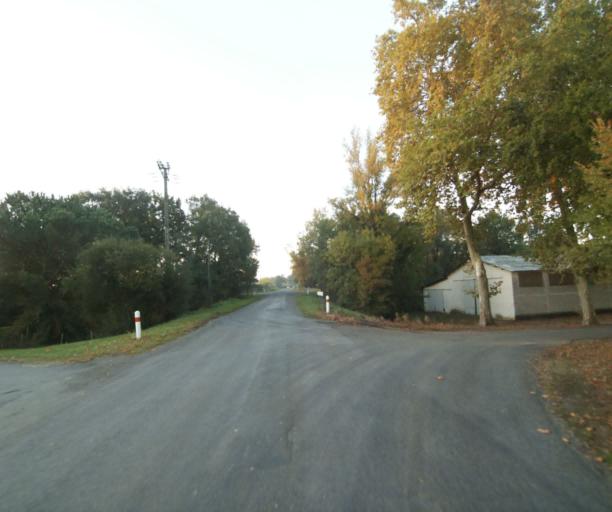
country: FR
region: Midi-Pyrenees
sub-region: Departement du Gers
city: Gondrin
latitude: 43.7959
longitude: 0.2258
